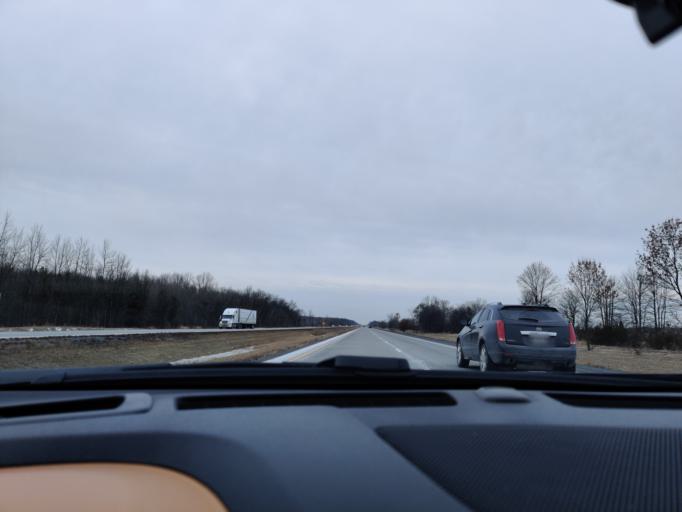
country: US
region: New York
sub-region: St. Lawrence County
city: Massena
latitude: 45.0343
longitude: -74.9398
